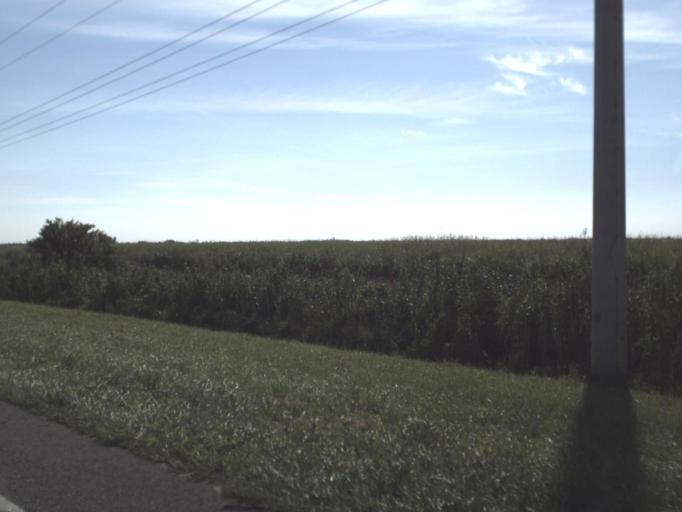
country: US
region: Florida
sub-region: Glades County
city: Moore Haven
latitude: 26.7923
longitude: -81.0829
